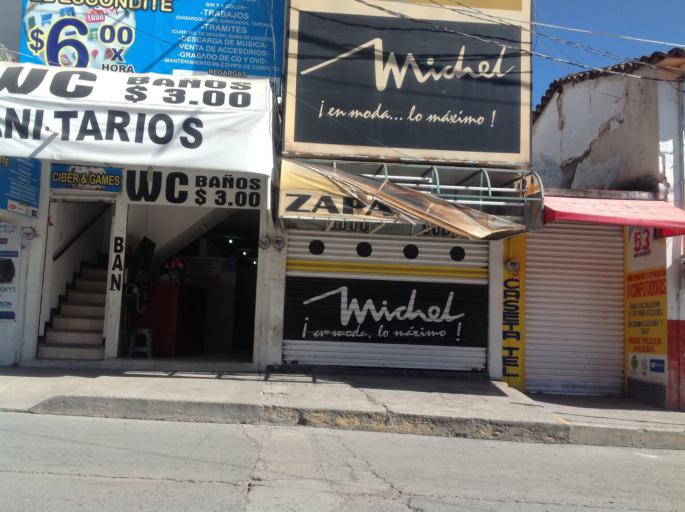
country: MX
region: Oaxaca
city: Ciudad de Huajuapam de Leon
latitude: 17.8078
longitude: -97.7757
